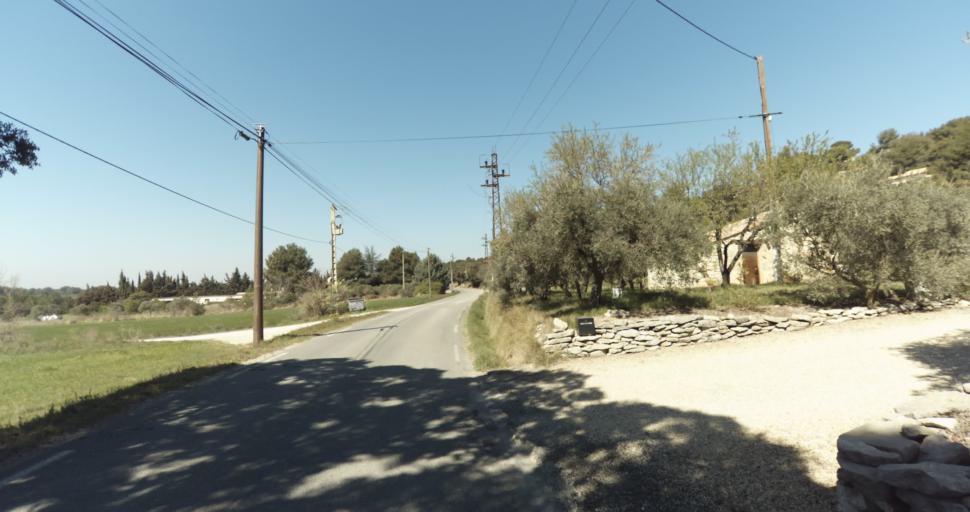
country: FR
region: Provence-Alpes-Cote d'Azur
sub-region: Departement des Bouches-du-Rhone
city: Pelissanne
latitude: 43.6113
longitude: 5.1755
